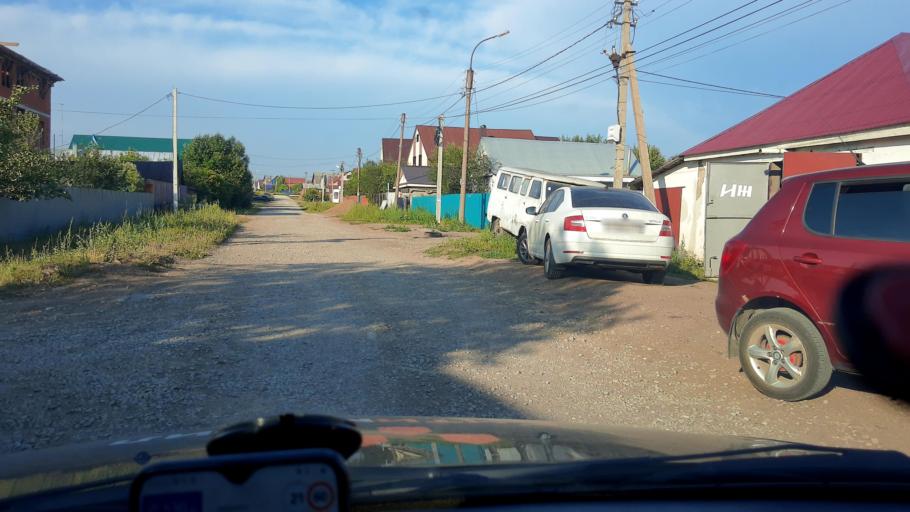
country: RU
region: Bashkortostan
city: Iglino
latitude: 54.7841
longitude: 56.2361
